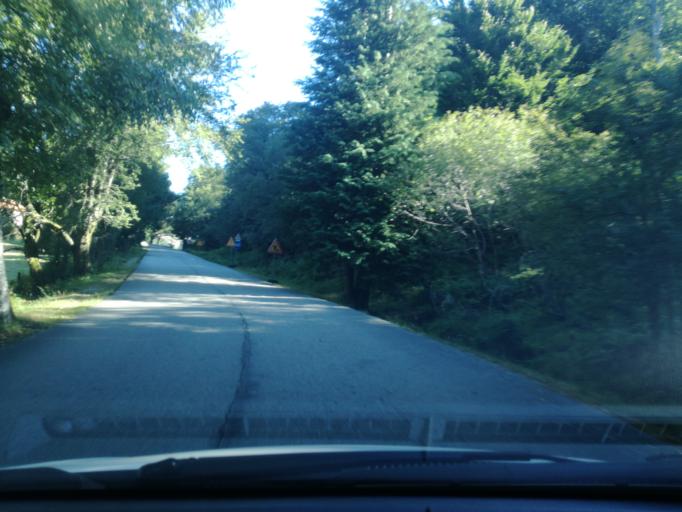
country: ES
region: Galicia
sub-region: Provincia de Ourense
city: Lobios
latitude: 41.7662
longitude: -8.1468
